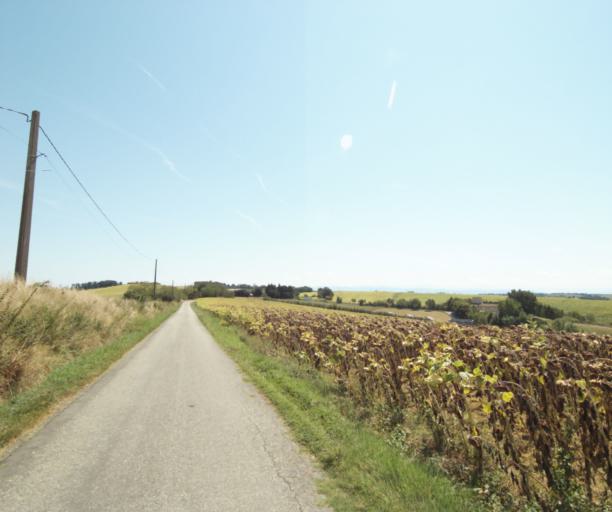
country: FR
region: Midi-Pyrenees
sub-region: Departement de la Haute-Garonne
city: Saint-Sulpice-sur-Leze
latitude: 43.2882
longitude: 1.3011
